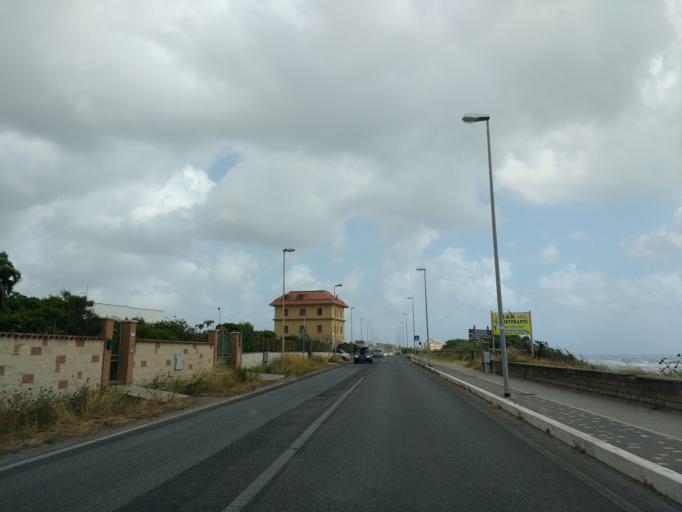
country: IT
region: Latium
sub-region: Citta metropolitana di Roma Capitale
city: Anzio
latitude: 41.4742
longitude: 12.6040
